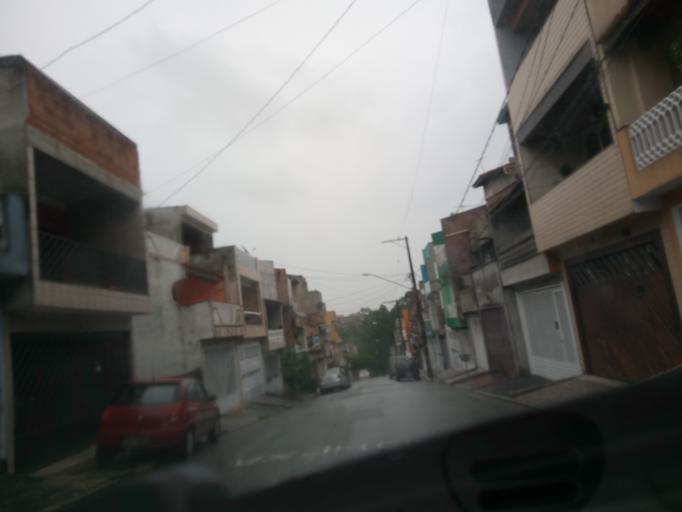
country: BR
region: Sao Paulo
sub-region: Sao Bernardo Do Campo
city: Sao Bernardo do Campo
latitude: -23.7178
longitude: -46.5963
